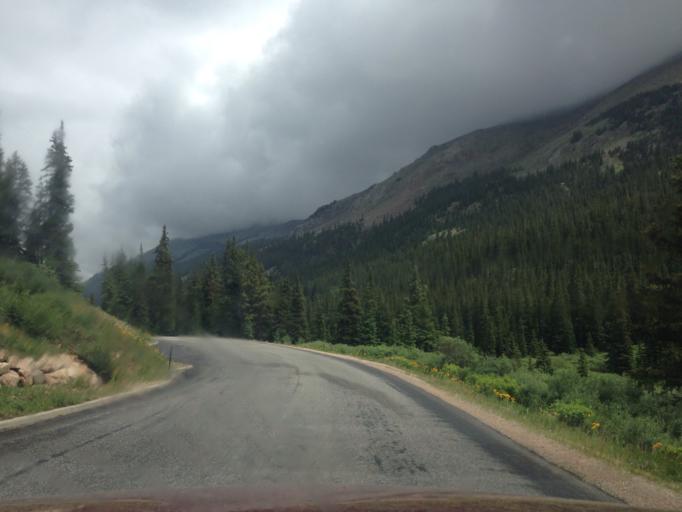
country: US
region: Colorado
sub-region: Clear Creek County
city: Georgetown
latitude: 39.6196
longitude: -105.7146
